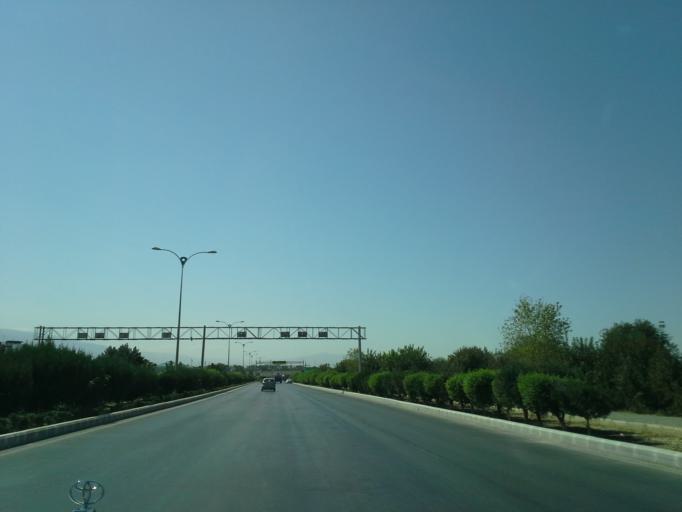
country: TM
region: Ahal
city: Annau
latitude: 37.9116
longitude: 58.4944
